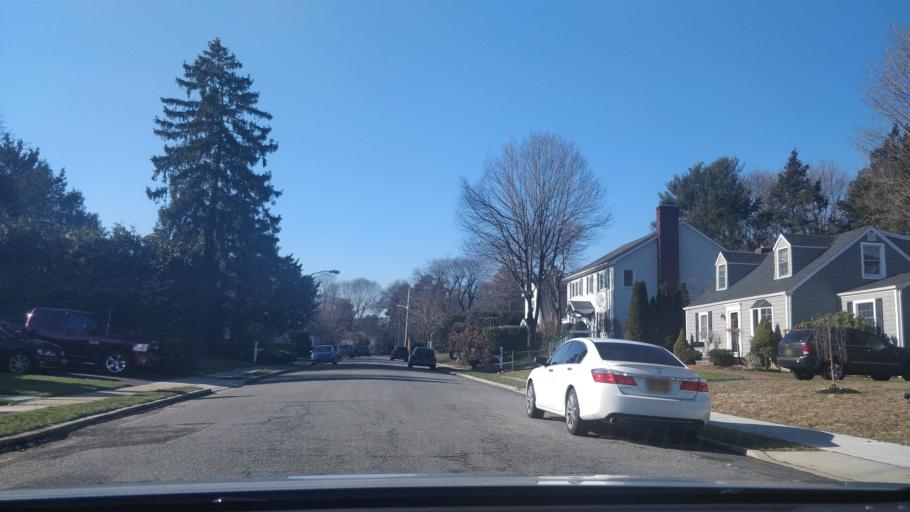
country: US
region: New York
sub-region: Nassau County
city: Locust Valley
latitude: 40.8810
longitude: -73.5819
